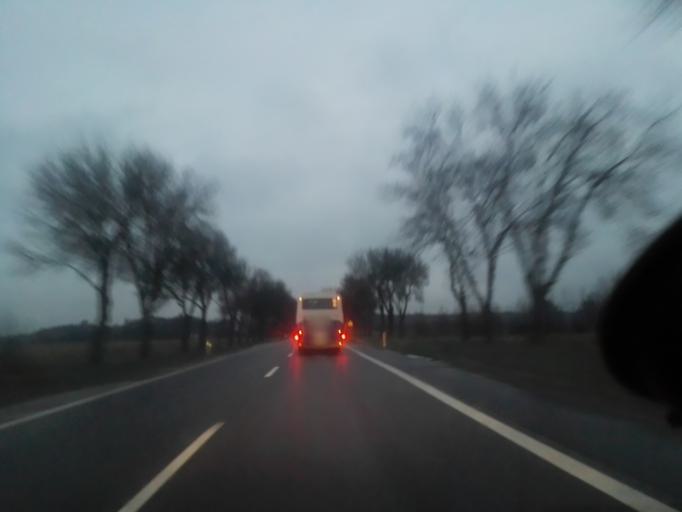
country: PL
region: Masovian Voivodeship
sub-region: Powiat wyszkowski
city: Branszczyk
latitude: 52.6814
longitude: 21.6251
